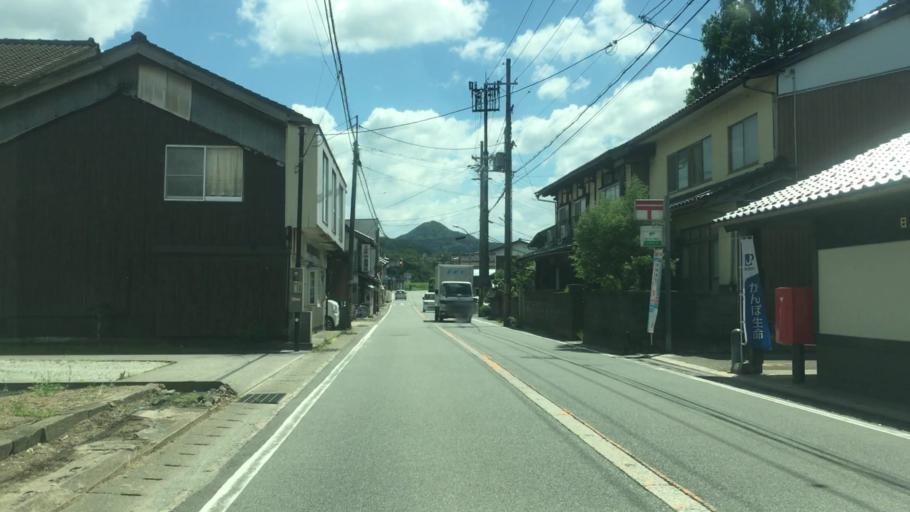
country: JP
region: Hyogo
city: Toyooka
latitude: 35.4854
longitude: 134.7987
